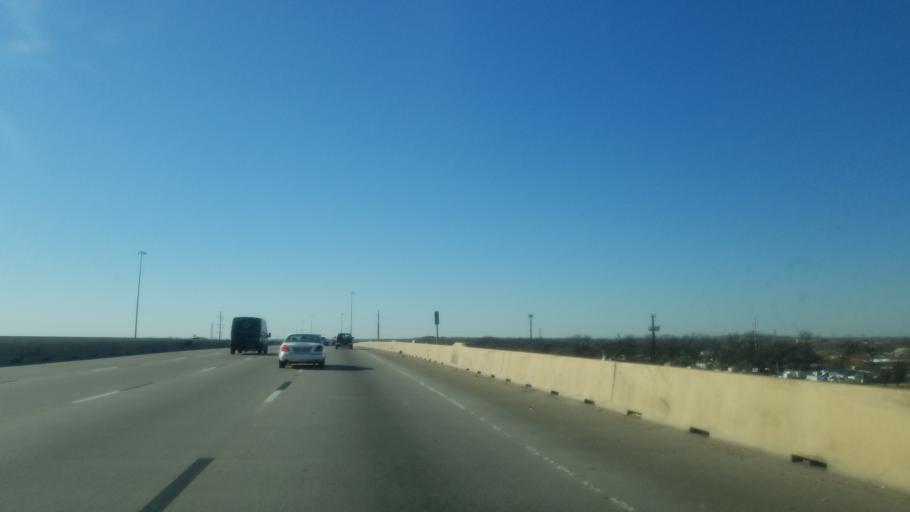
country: US
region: Texas
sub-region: Dallas County
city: Cockrell Hill
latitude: 32.7667
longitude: -96.9128
